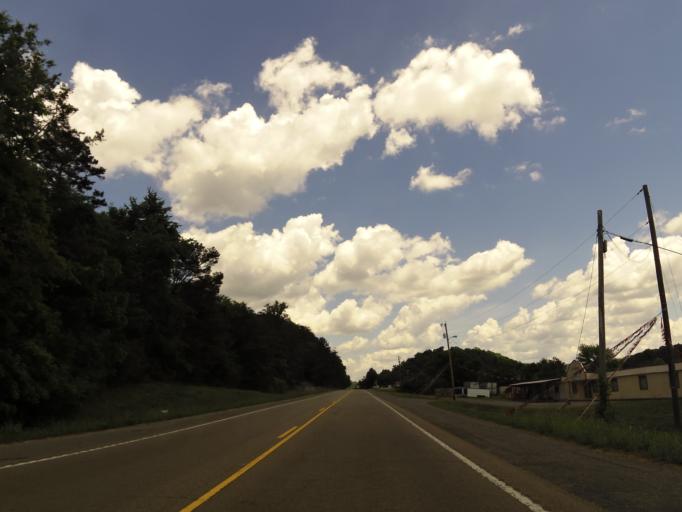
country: US
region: Tennessee
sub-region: Union County
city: Condon
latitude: 36.2001
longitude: -83.8800
